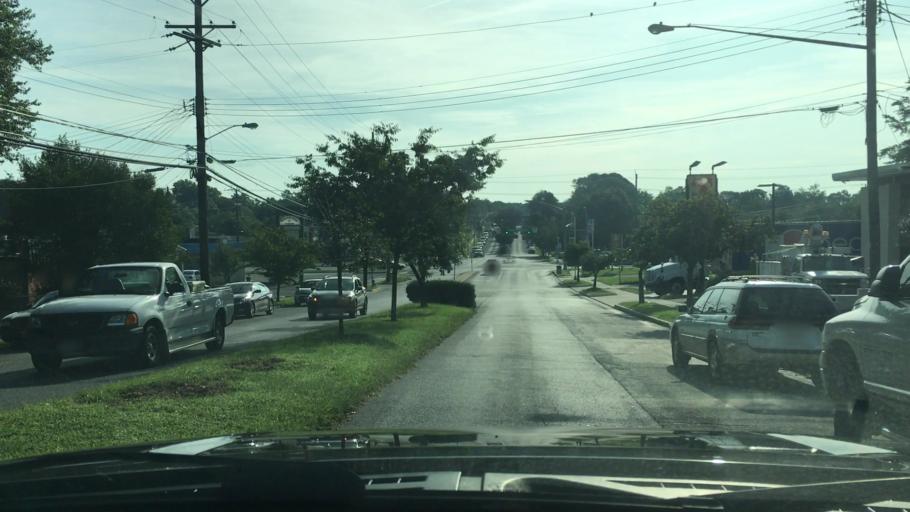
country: US
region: Maryland
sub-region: Prince George's County
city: Beltsville
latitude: 39.0159
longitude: -76.9224
